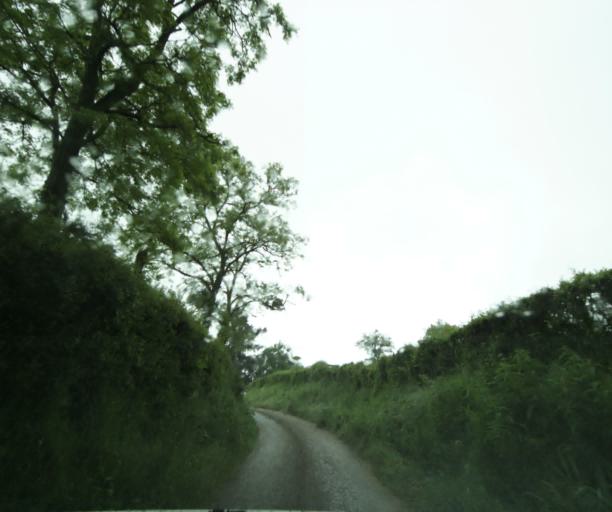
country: FR
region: Bourgogne
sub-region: Departement de Saone-et-Loire
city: Matour
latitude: 46.3691
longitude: 4.3921
